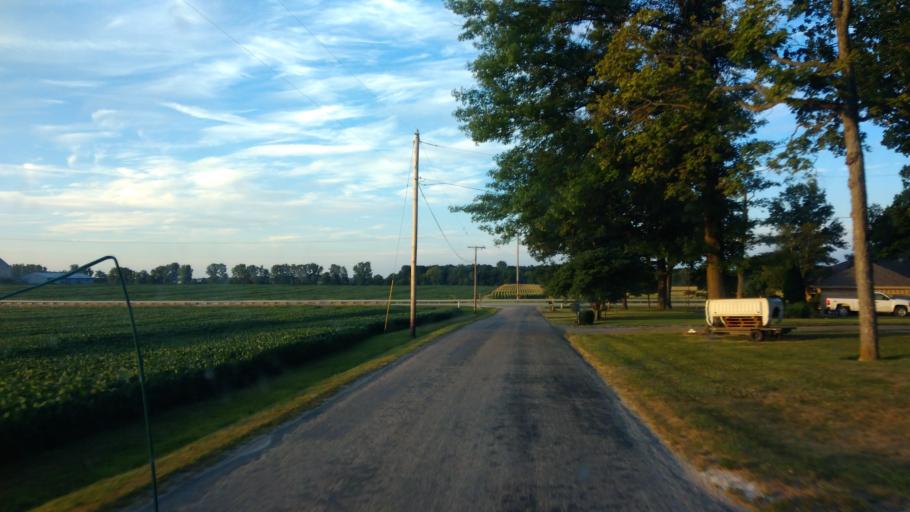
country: US
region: Indiana
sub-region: Adams County
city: Berne
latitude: 40.6574
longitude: -85.0228
